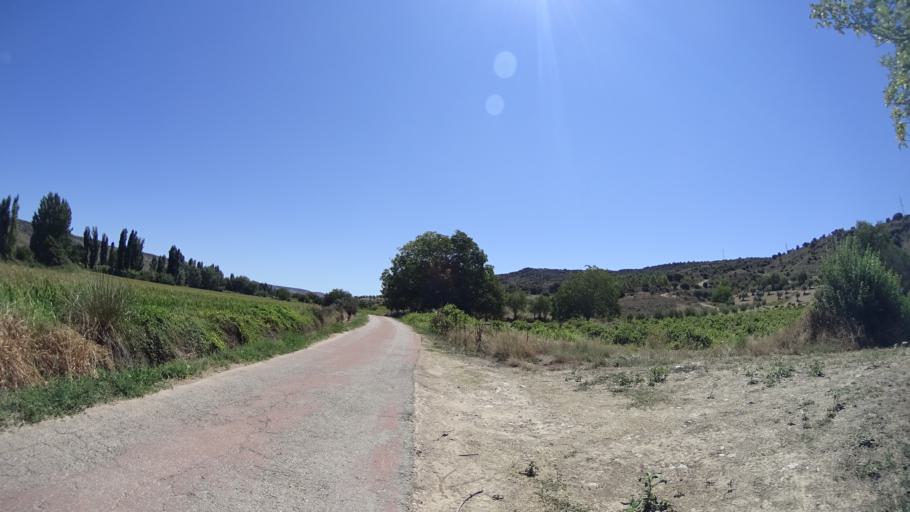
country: ES
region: Madrid
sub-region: Provincia de Madrid
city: Tielmes
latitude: 40.2422
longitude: -3.2866
